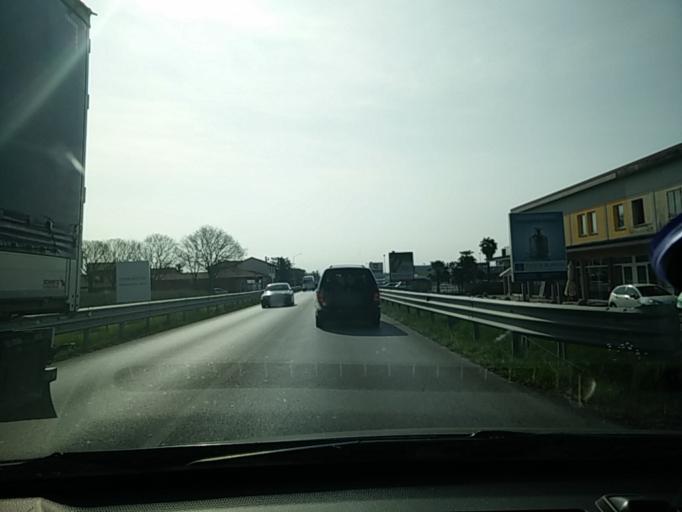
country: IT
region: Friuli Venezia Giulia
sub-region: Provincia di Udine
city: Buttrio
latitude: 46.0125
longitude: 13.3235
